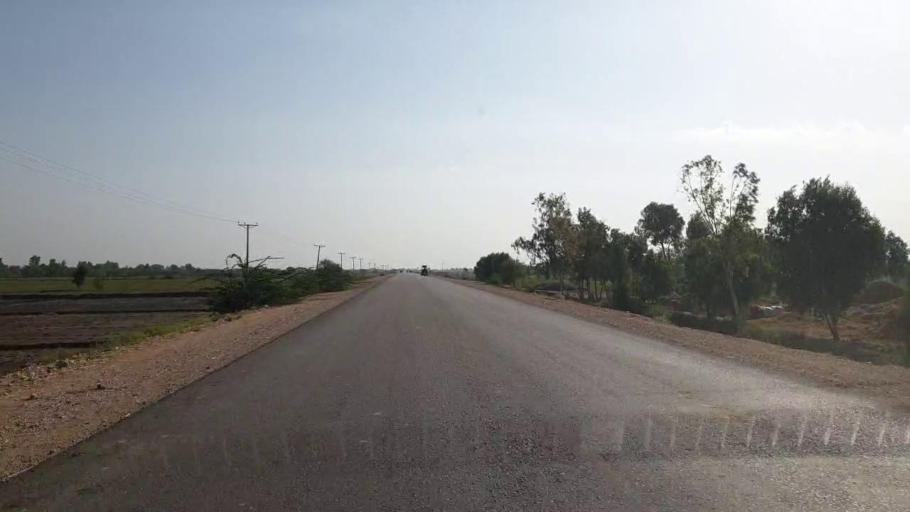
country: PK
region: Sindh
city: Tando Bago
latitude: 24.6569
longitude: 69.0114
